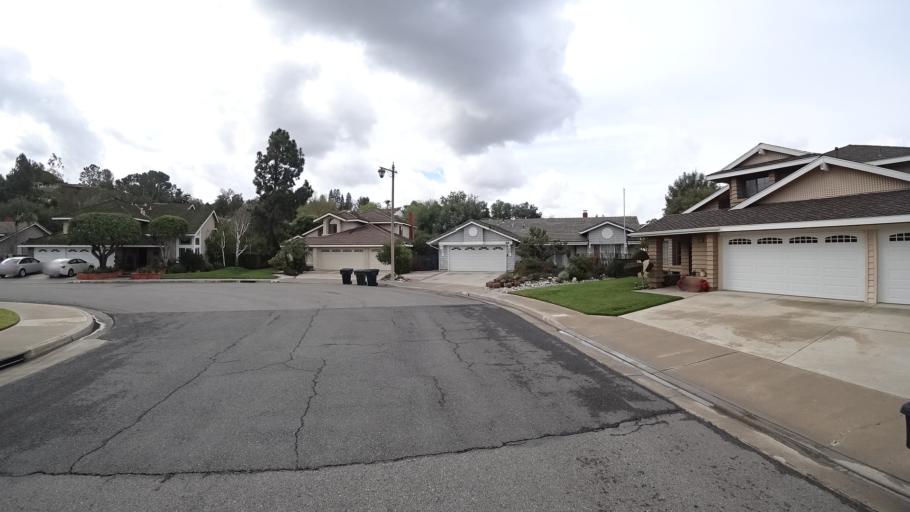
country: US
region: California
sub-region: Orange County
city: Yorba Linda
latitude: 33.8524
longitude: -117.7752
